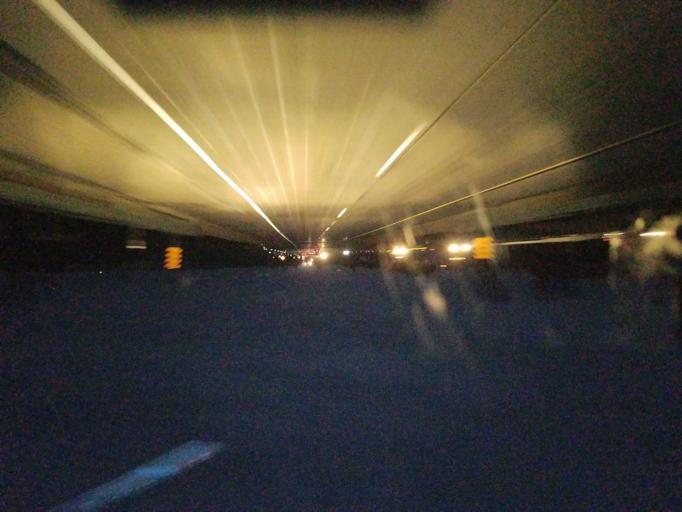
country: US
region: Iowa
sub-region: Guthrie County
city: Guthrie Center
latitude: 41.4961
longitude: -94.5205
